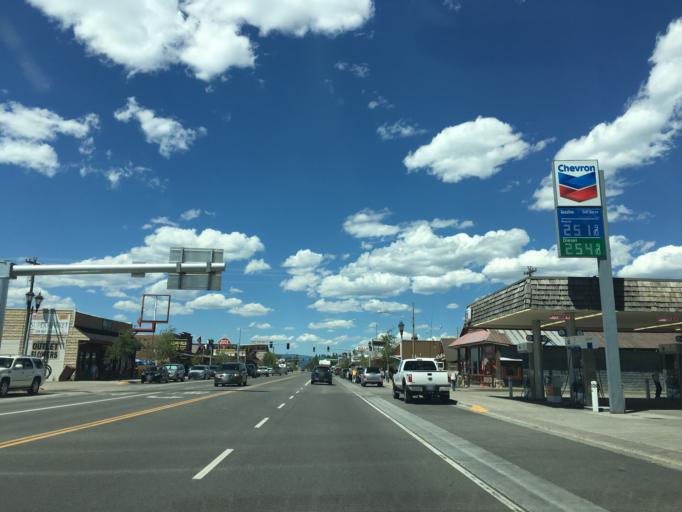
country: US
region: Montana
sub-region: Gallatin County
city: West Yellowstone
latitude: 44.6590
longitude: -111.0995
